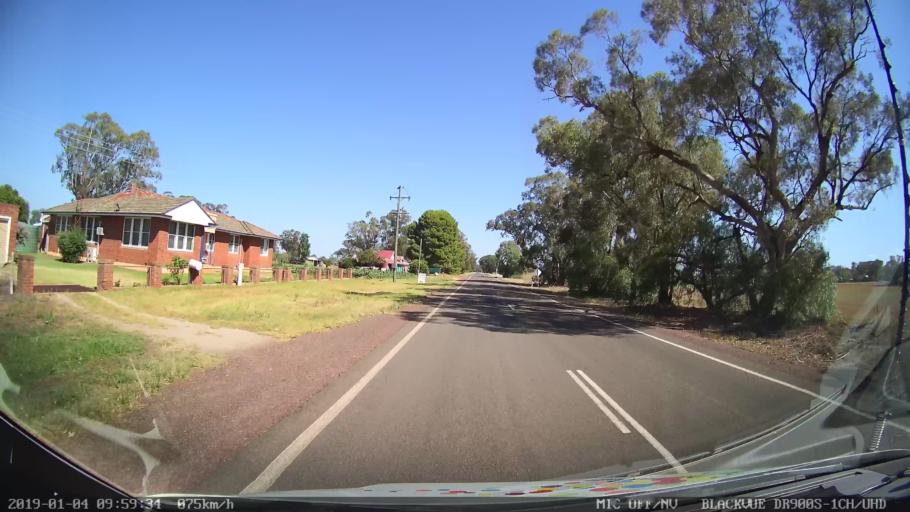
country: AU
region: New South Wales
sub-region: Cabonne
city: Canowindra
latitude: -33.5062
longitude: 148.3853
